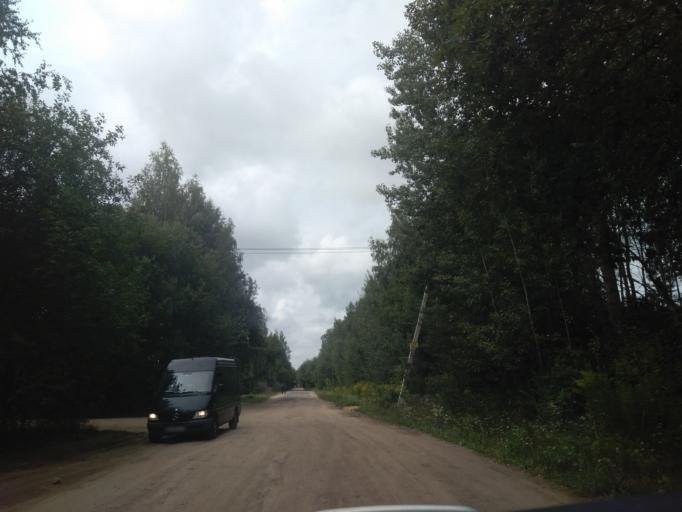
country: BY
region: Minsk
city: Slabada
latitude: 53.9936
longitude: 27.9099
